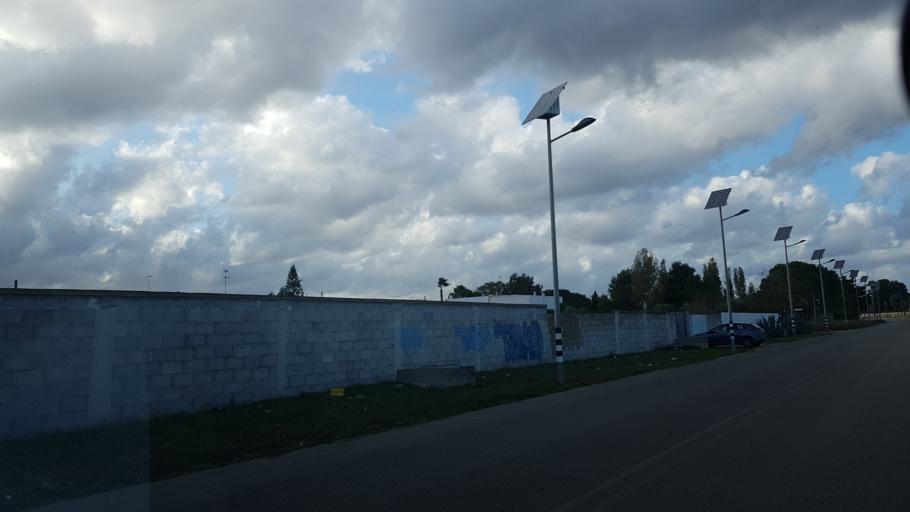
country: IT
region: Apulia
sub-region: Provincia di Brindisi
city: San Pietro Vernotico
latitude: 40.4964
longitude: 18.0069
